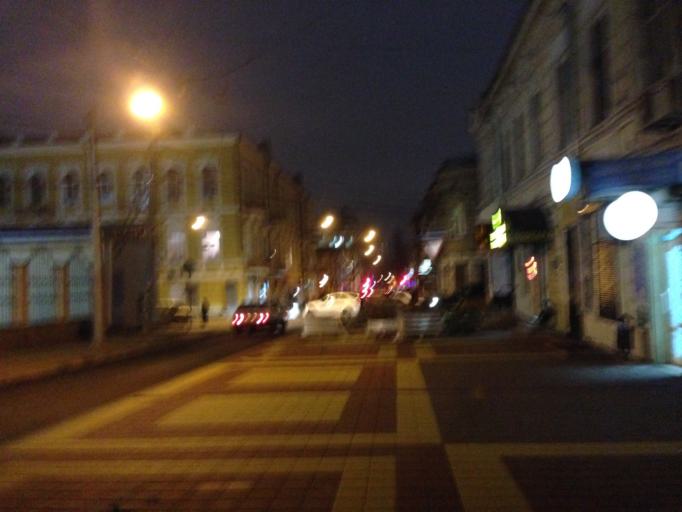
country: RU
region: Rostov
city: Rostov-na-Donu
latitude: 47.2203
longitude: 39.7165
